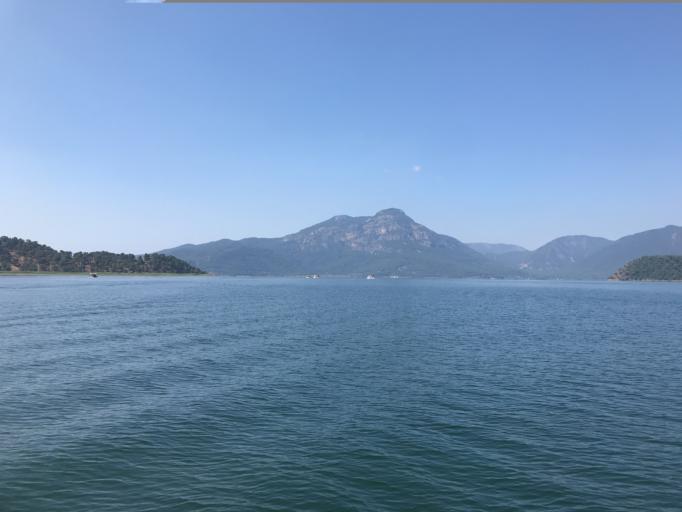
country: TR
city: Dalyan
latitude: 36.9076
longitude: 28.6507
